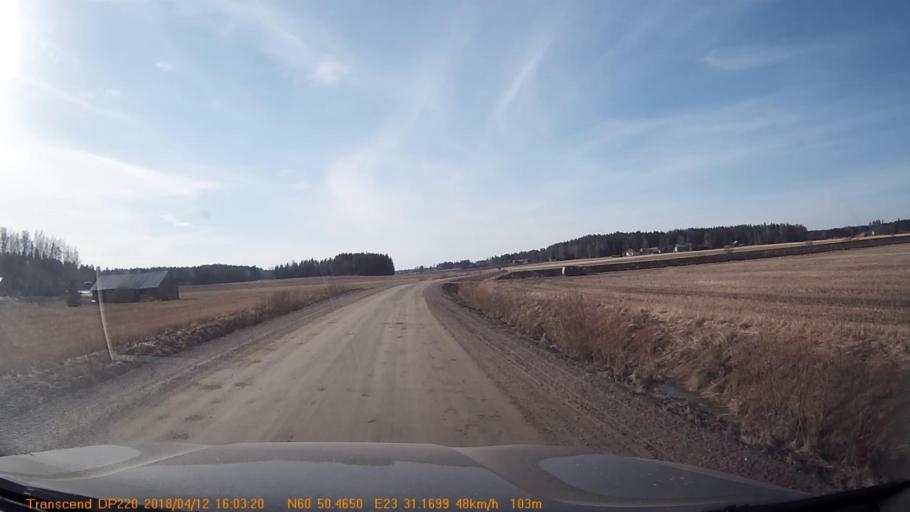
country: FI
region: Haeme
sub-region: Forssa
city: Jokioinen
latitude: 60.8412
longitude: 23.5192
